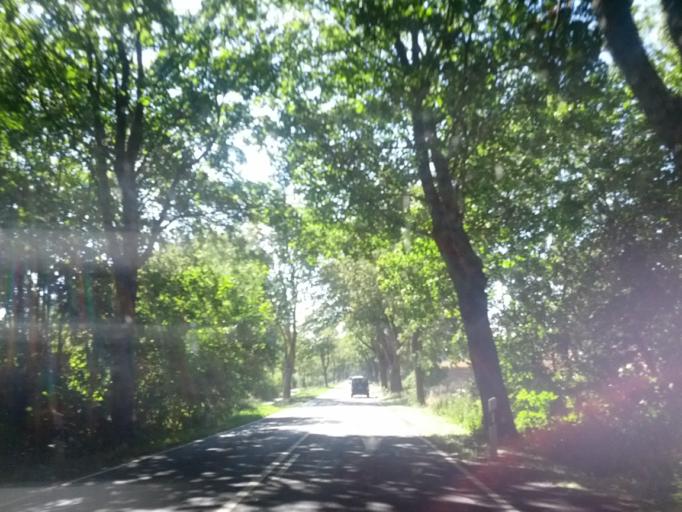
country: DE
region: Mecklenburg-Vorpommern
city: Bergen auf Ruegen
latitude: 54.4480
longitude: 13.4386
